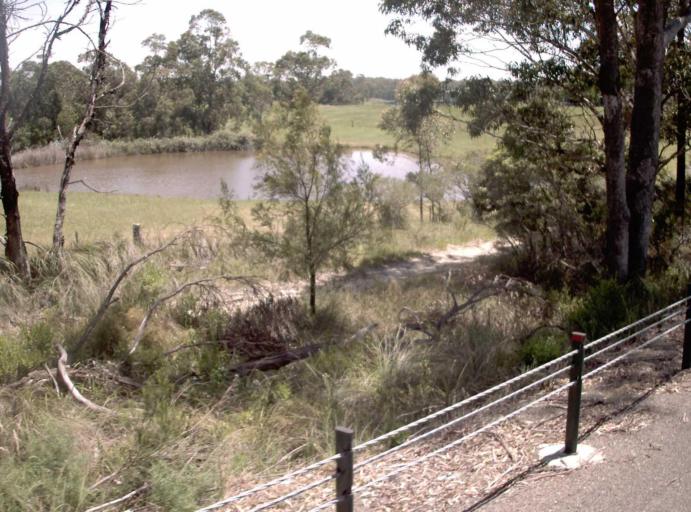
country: AU
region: Victoria
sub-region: East Gippsland
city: Lakes Entrance
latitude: -37.8343
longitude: 148.0313
